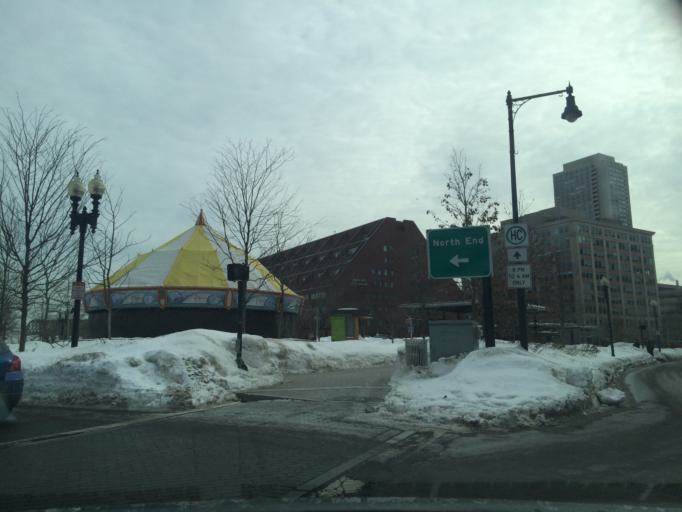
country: US
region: Massachusetts
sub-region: Suffolk County
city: Boston
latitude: 42.3606
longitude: -71.0532
